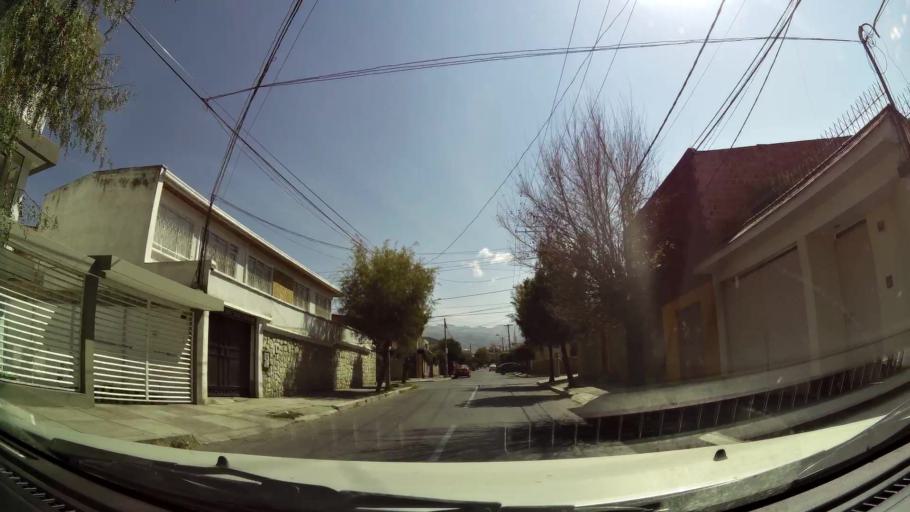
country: BO
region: La Paz
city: La Paz
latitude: -16.5282
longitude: -68.0849
